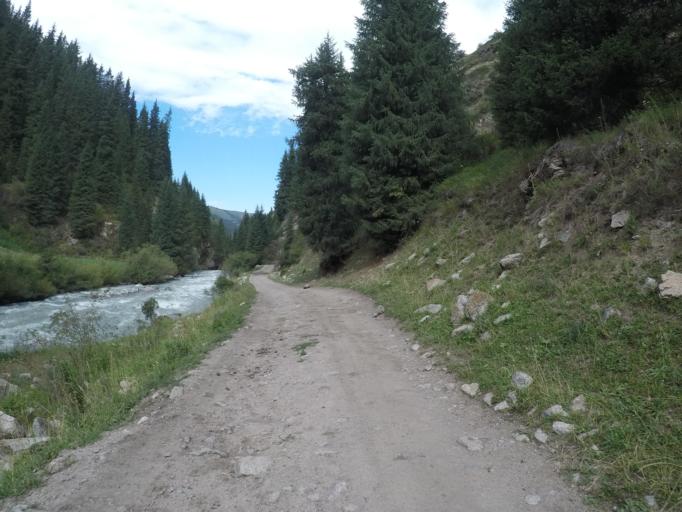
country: KG
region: Ysyk-Koel
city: Teploklyuchenka
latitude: 42.4416
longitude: 78.5555
